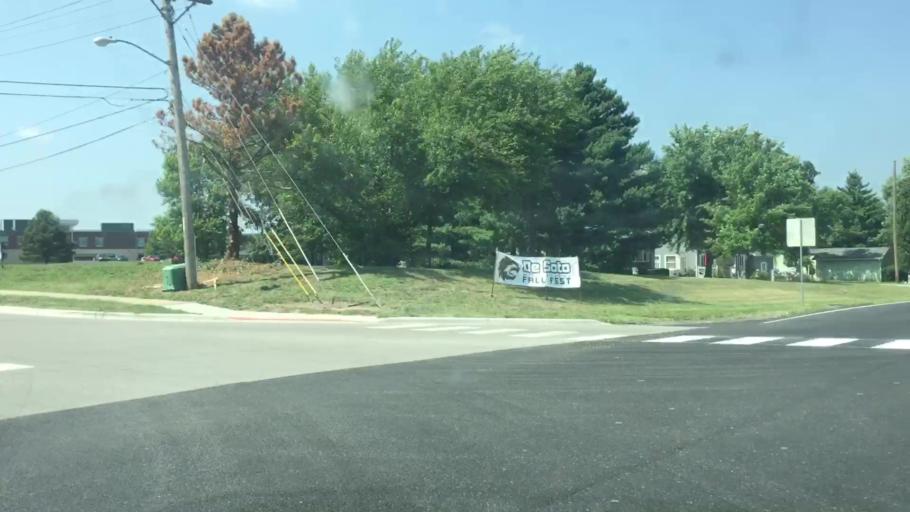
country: US
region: Kansas
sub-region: Johnson County
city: De Soto
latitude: 38.9640
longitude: -94.9831
